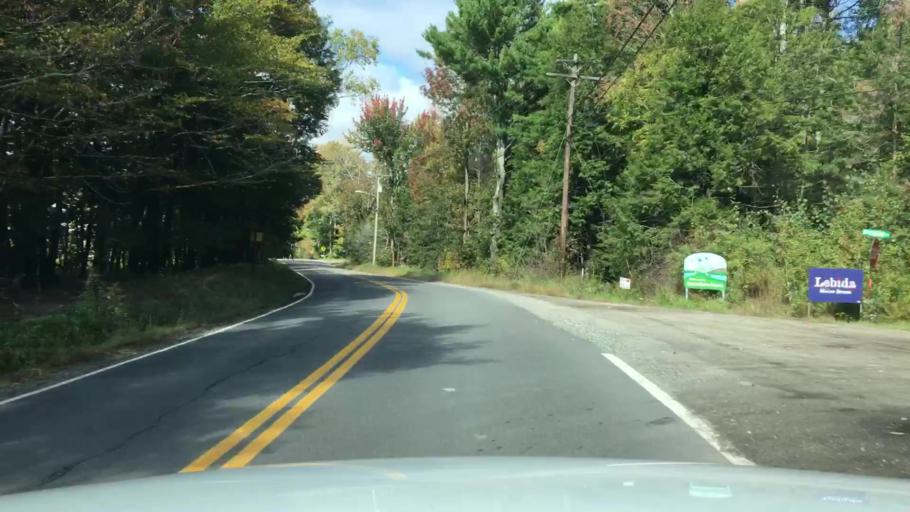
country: US
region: Maine
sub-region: Sagadahoc County
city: North Bath
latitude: 44.0034
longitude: -69.8907
